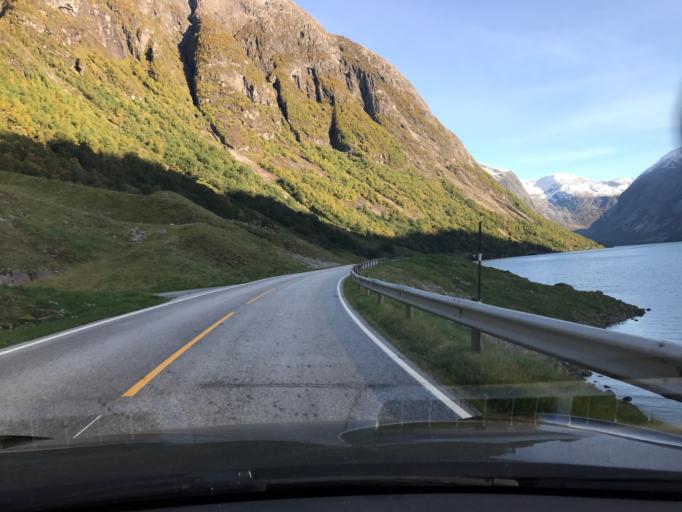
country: NO
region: Sogn og Fjordane
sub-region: Jolster
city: Skei
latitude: 61.5432
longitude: 6.5152
